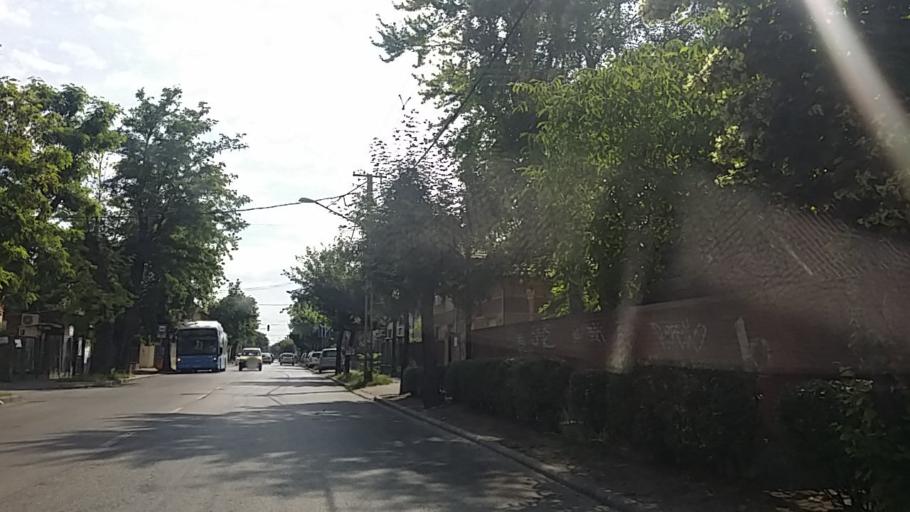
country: HU
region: Budapest
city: Budapest XX. keruelet
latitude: 47.4442
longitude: 19.1235
